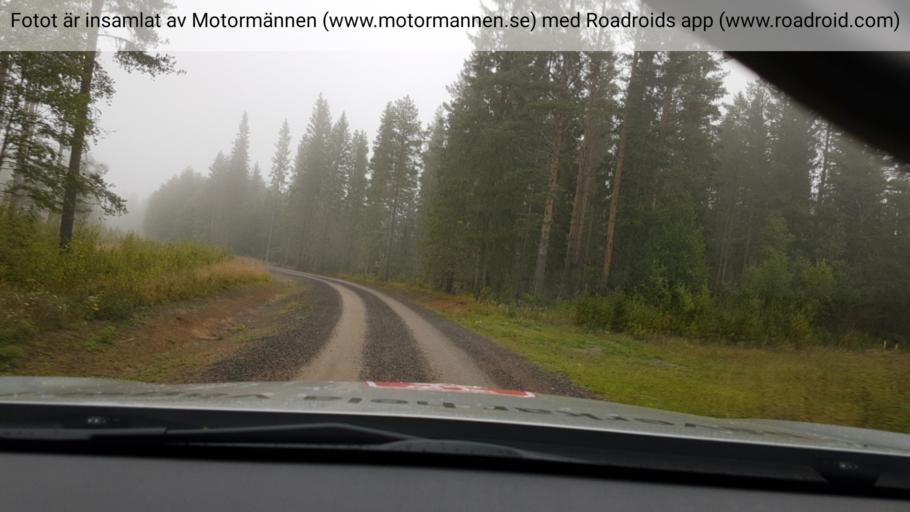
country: SE
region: Vaesterbotten
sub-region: Umea Kommun
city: Ersmark
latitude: 64.1497
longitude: 20.3947
